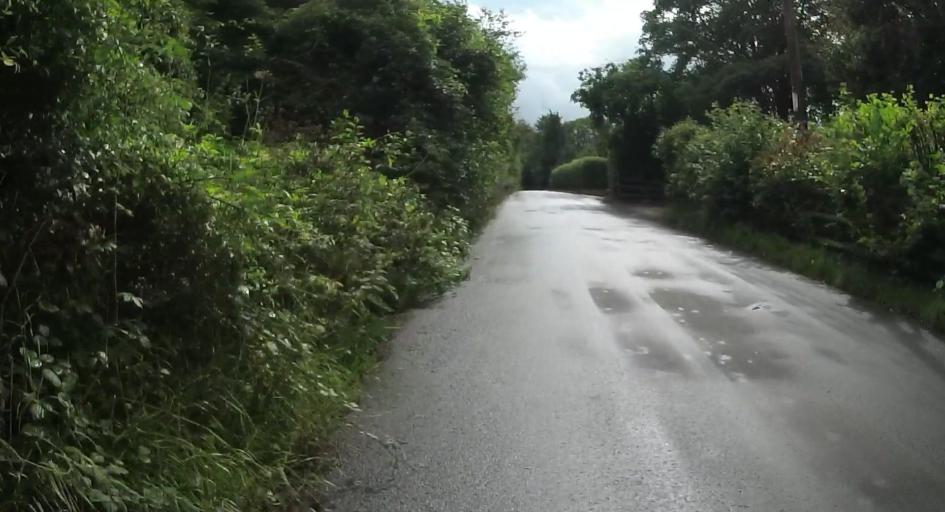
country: GB
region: England
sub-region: Hampshire
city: Andover
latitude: 51.2206
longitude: -1.4347
